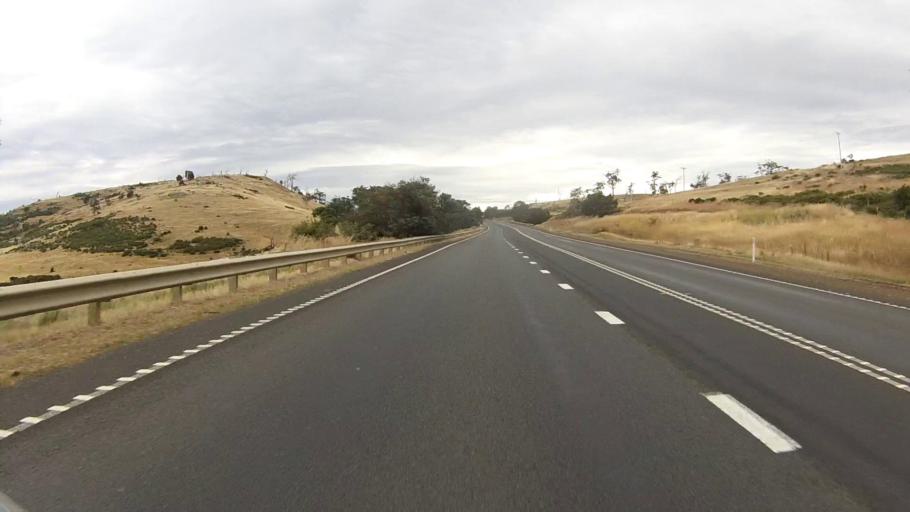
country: AU
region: Tasmania
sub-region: Brighton
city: Bridgewater
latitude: -42.3413
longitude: 147.3400
